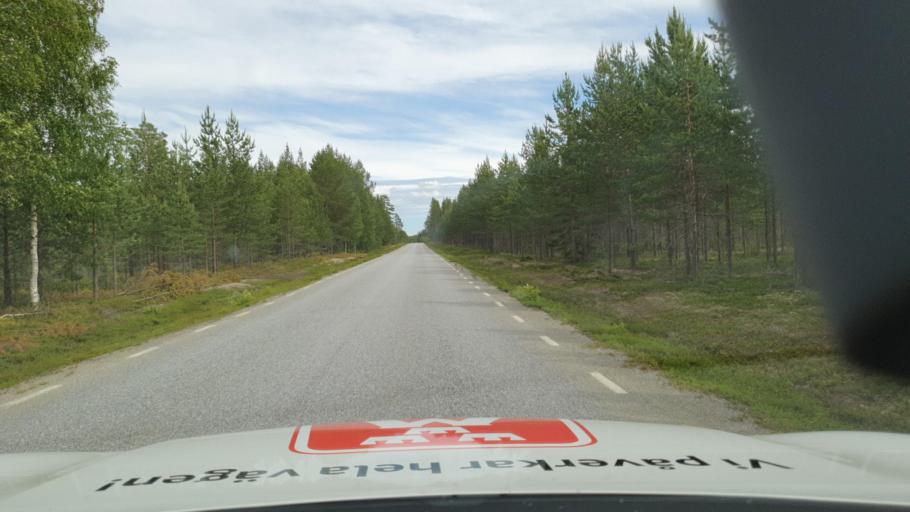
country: SE
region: Vaesterbotten
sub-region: Skelleftea Kommun
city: Burtraesk
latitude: 64.5045
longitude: 20.8128
